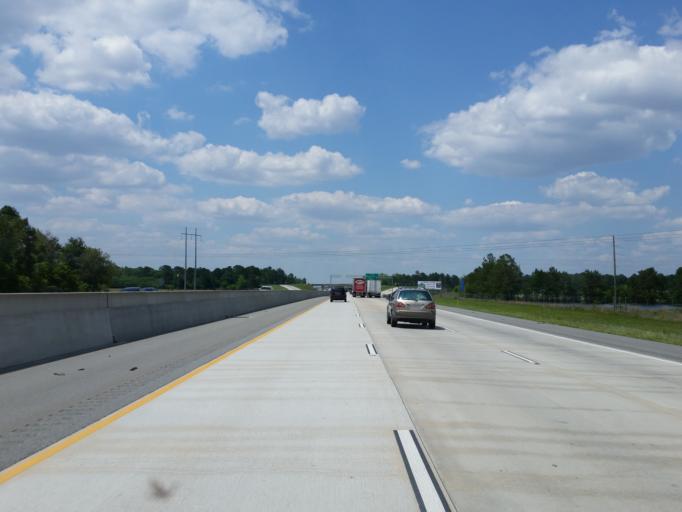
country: US
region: Georgia
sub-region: Cook County
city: Sparks
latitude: 31.2085
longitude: -83.4588
